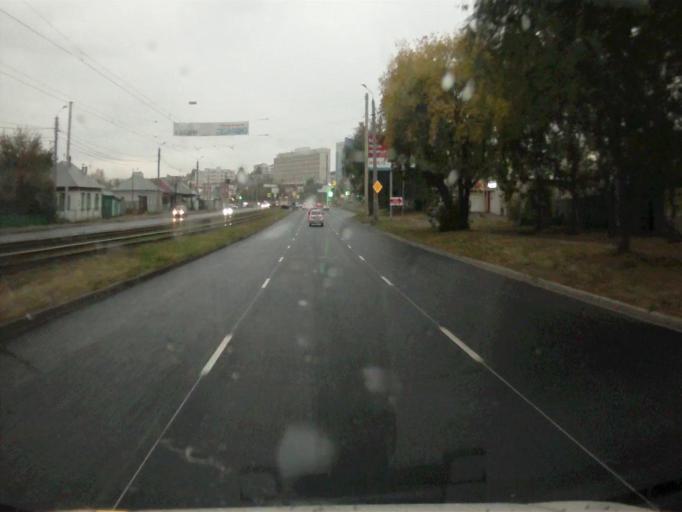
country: RU
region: Chelyabinsk
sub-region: Gorod Chelyabinsk
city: Chelyabinsk
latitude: 55.1870
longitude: 61.3633
